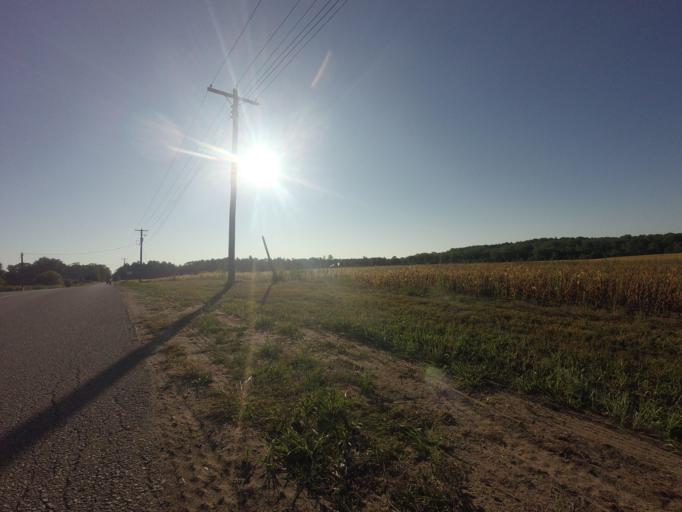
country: CA
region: Ontario
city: Bradford West Gwillimbury
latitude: 44.0479
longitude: -79.7472
